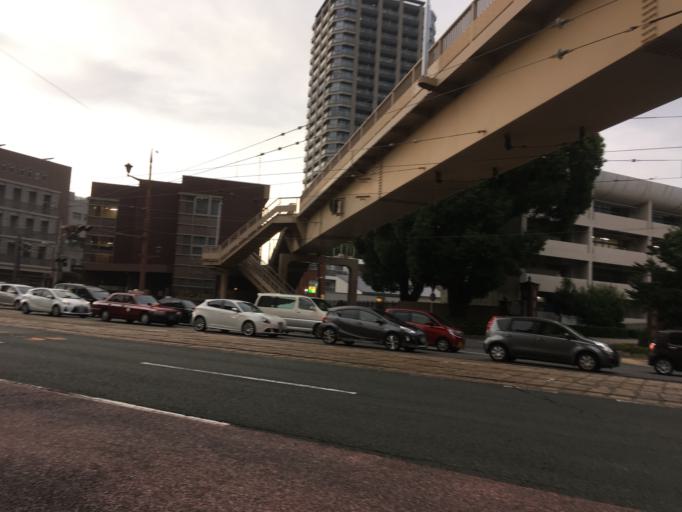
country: JP
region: Kumamoto
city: Kumamoto
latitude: 32.7973
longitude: 130.7202
